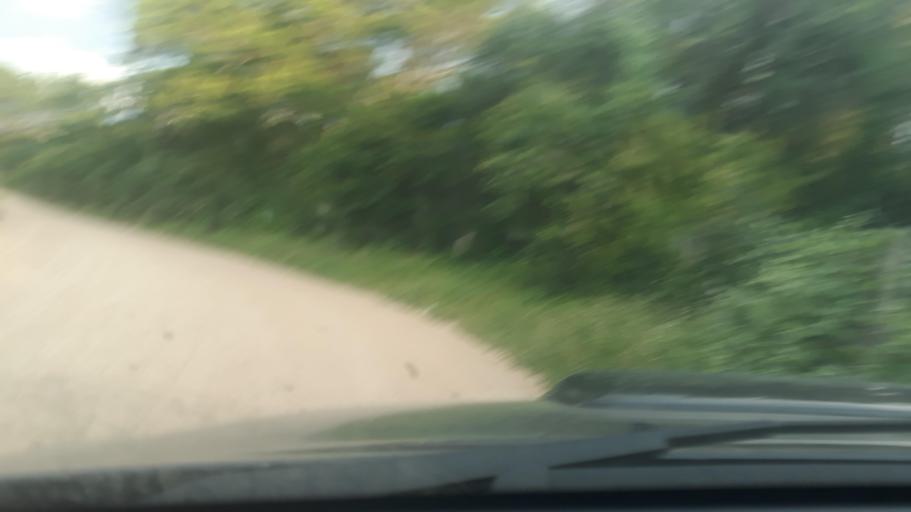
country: BR
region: Bahia
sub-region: Riacho De Santana
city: Riacho de Santana
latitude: -13.9102
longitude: -42.9411
